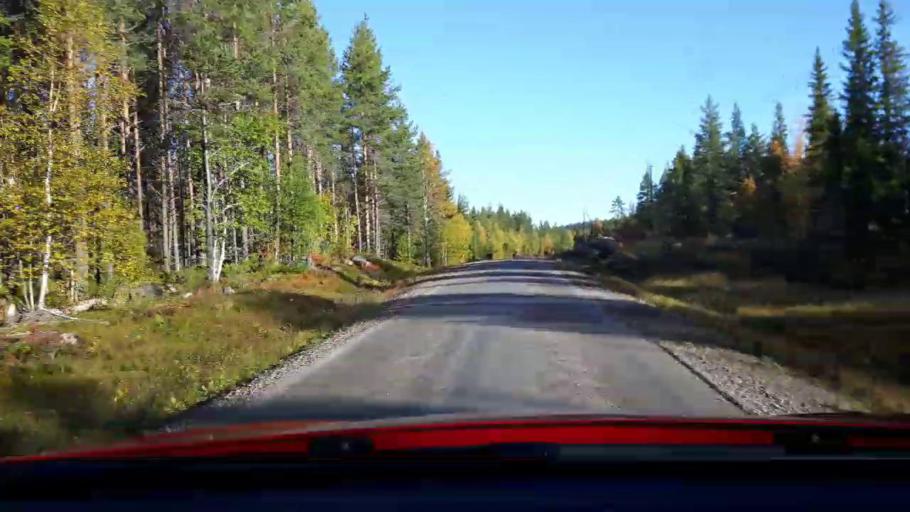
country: SE
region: Jaemtland
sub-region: Stroemsunds Kommun
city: Stroemsund
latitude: 64.3896
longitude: 15.1504
